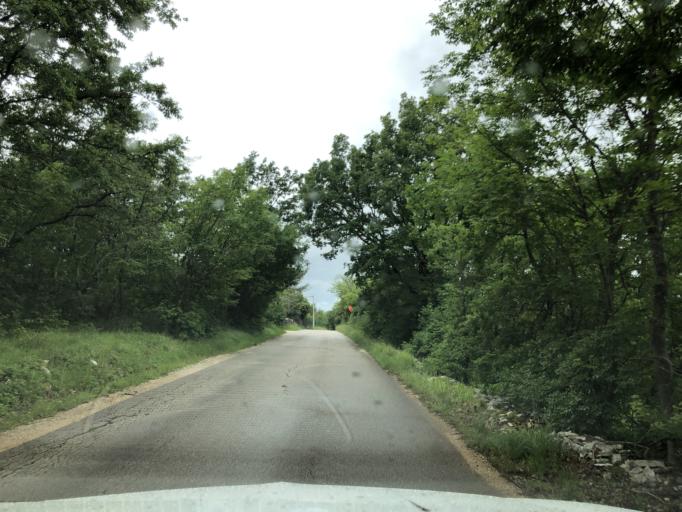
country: HR
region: Istarska
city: Buje
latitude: 45.4369
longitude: 13.6693
